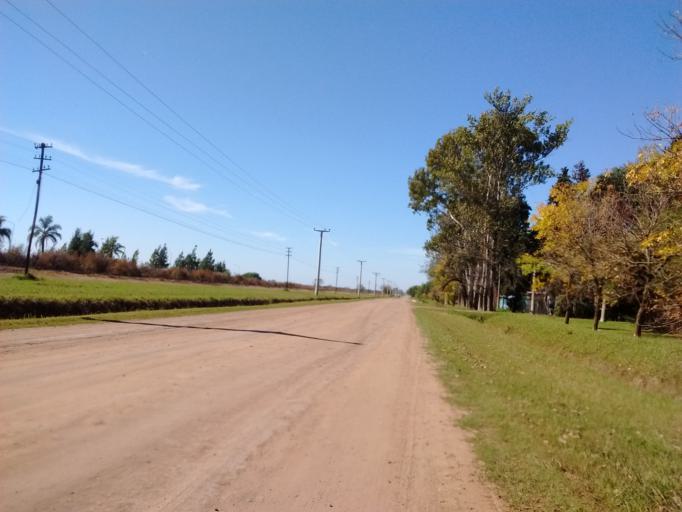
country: AR
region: Santa Fe
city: Roldan
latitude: -32.9086
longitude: -60.8593
